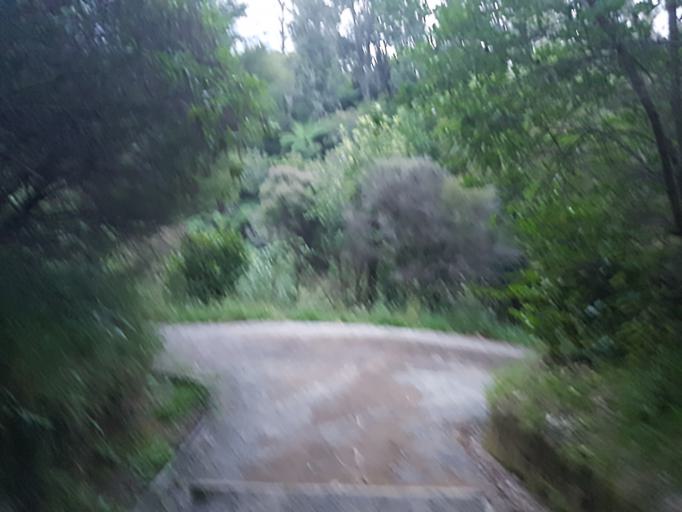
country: NZ
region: Bay of Plenty
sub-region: Tauranga City
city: Tauranga
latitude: -37.7603
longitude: 176.2415
